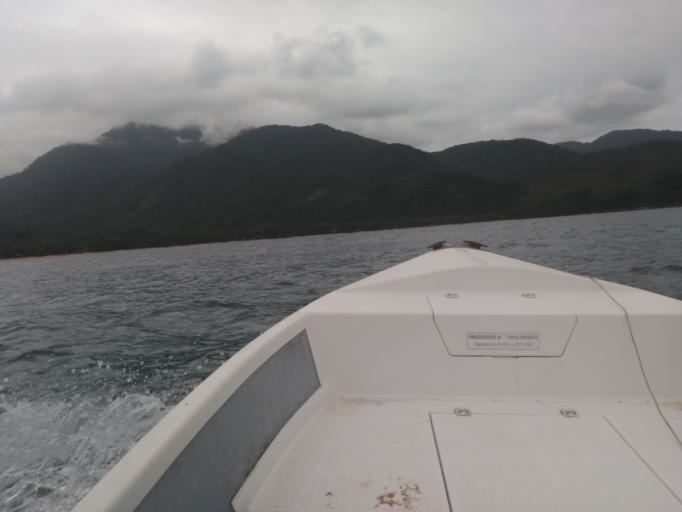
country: BR
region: Rio de Janeiro
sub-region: Parati
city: Paraty
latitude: -23.3385
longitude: -44.6391
